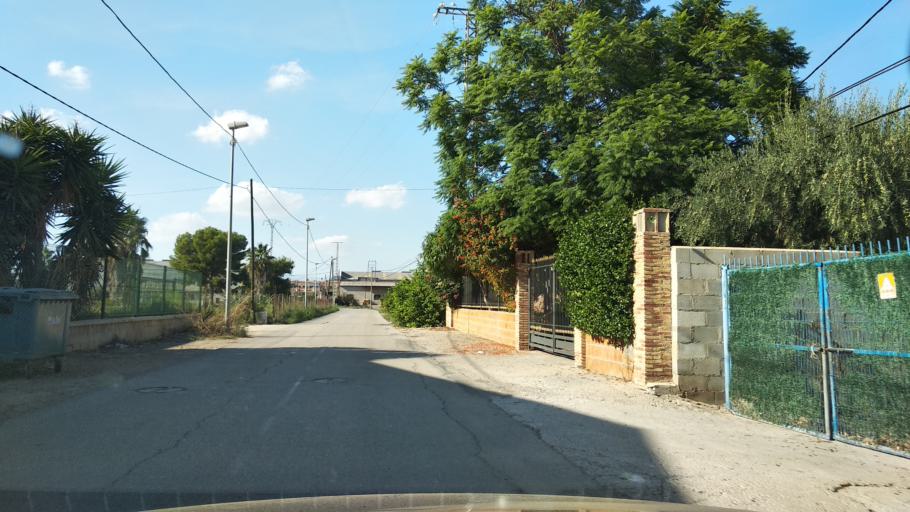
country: ES
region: Murcia
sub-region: Murcia
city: Santomera
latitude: 38.0545
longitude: -1.0423
